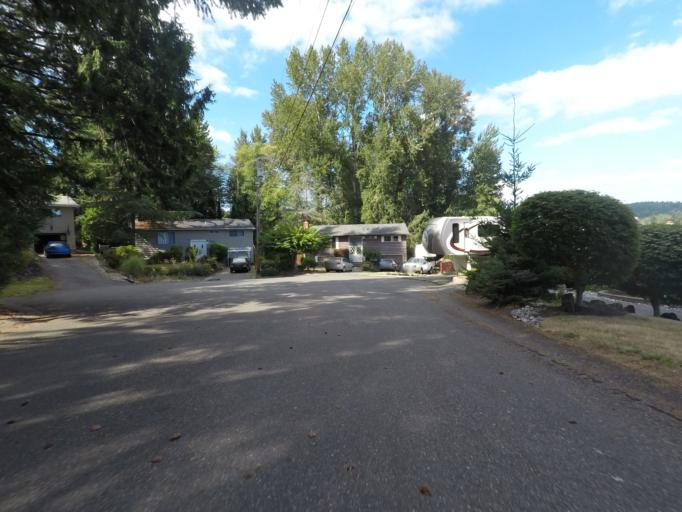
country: US
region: Washington
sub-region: Snohomish County
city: Brier
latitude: 47.7764
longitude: -122.2579
